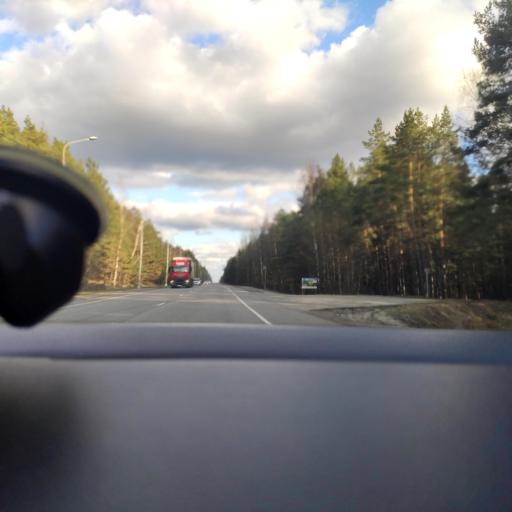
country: RU
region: Moskovskaya
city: Il'inskiy Pogost
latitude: 55.4714
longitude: 38.9605
